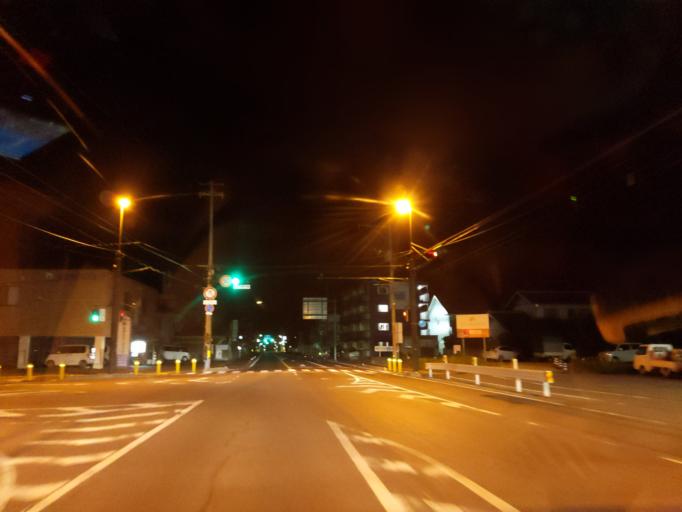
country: JP
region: Okayama
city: Okayama-shi
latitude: 34.6889
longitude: 133.9586
